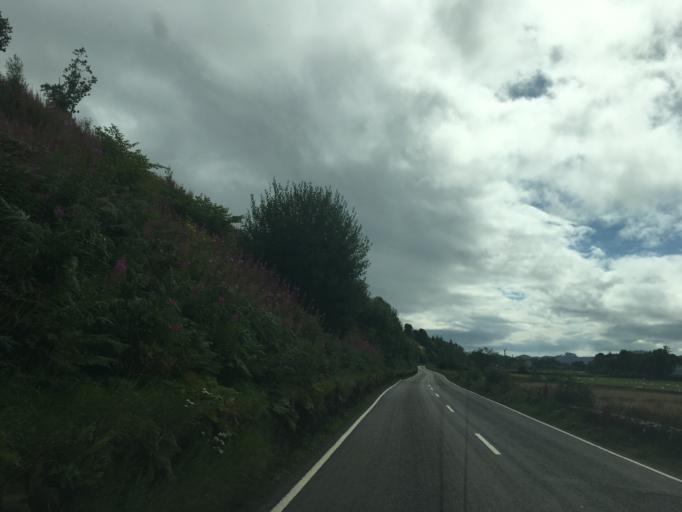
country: GB
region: Scotland
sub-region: Argyll and Bute
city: Lochgilphead
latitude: 56.1286
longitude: -5.4866
